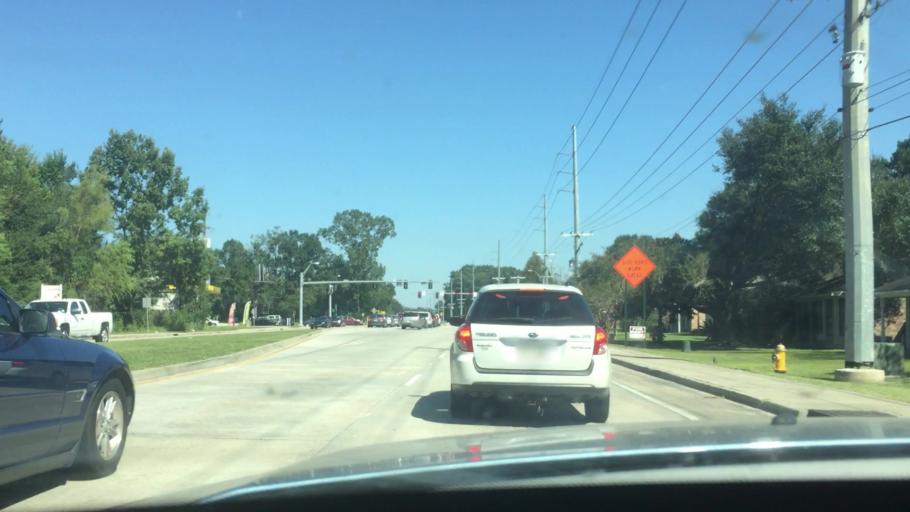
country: US
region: Louisiana
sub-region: East Baton Rouge Parish
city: Shenandoah
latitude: 30.4255
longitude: -91.0092
